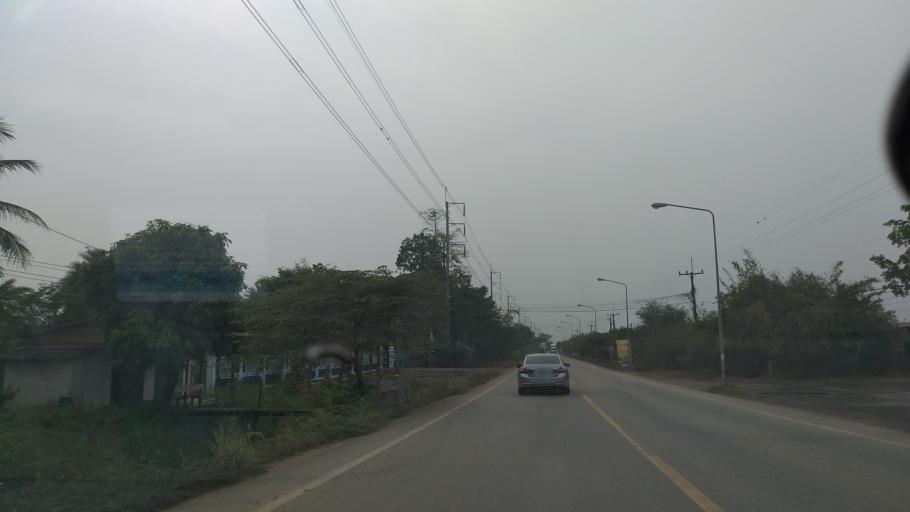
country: TH
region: Chachoengsao
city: Plaeng Yao
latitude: 13.5848
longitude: 101.2196
